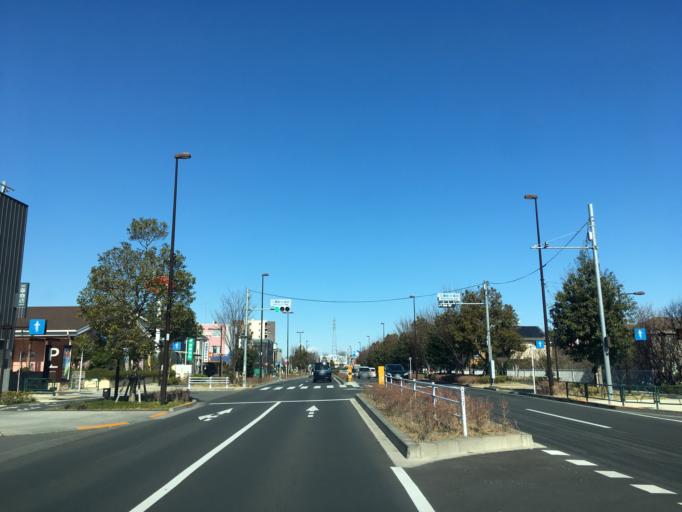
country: JP
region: Tokyo
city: Mitaka-shi
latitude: 35.6869
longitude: 139.5501
